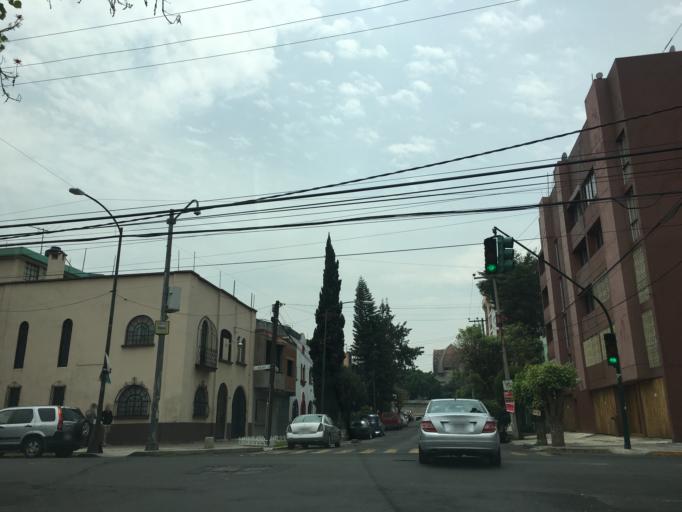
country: MX
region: Mexico City
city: Benito Juarez
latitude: 19.4047
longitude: -99.1593
